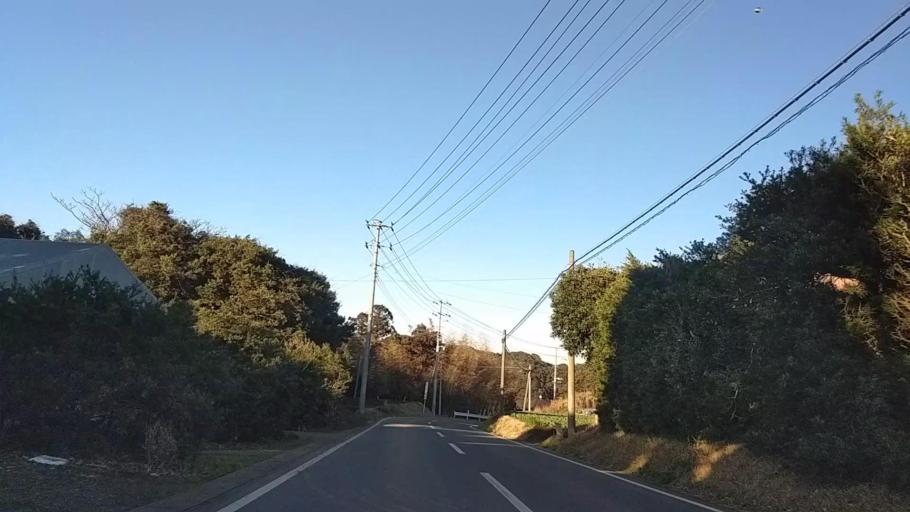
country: JP
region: Chiba
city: Asahi
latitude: 35.7173
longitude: 140.7316
